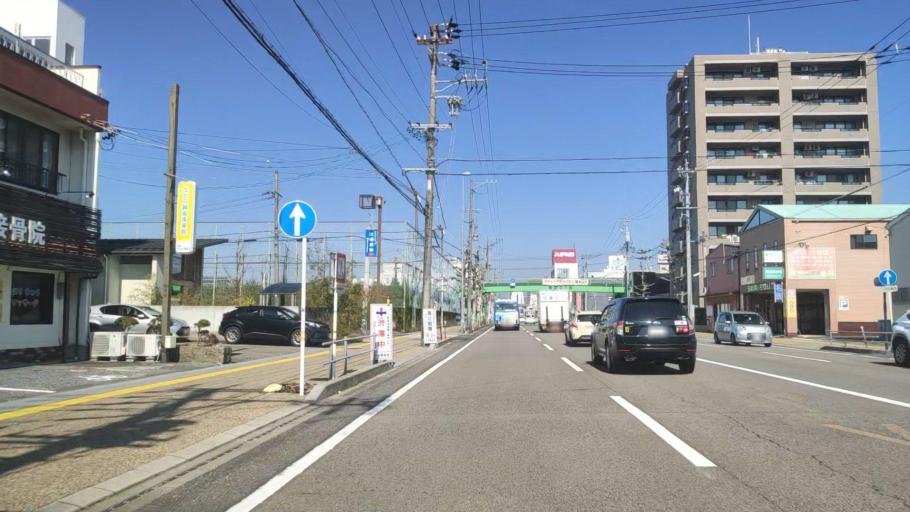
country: JP
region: Gifu
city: Gifu-shi
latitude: 35.4040
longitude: 136.7474
